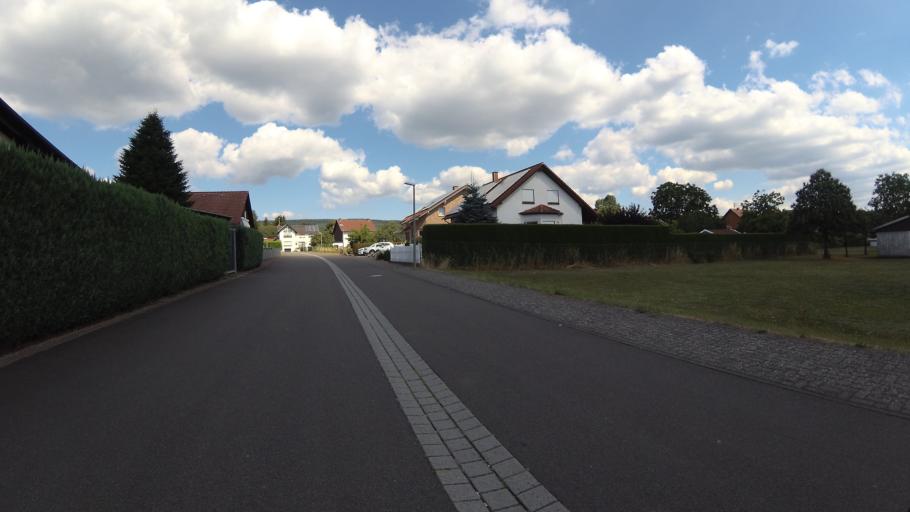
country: DE
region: Saarland
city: Weiskirchen
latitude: 49.5406
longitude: 6.7924
